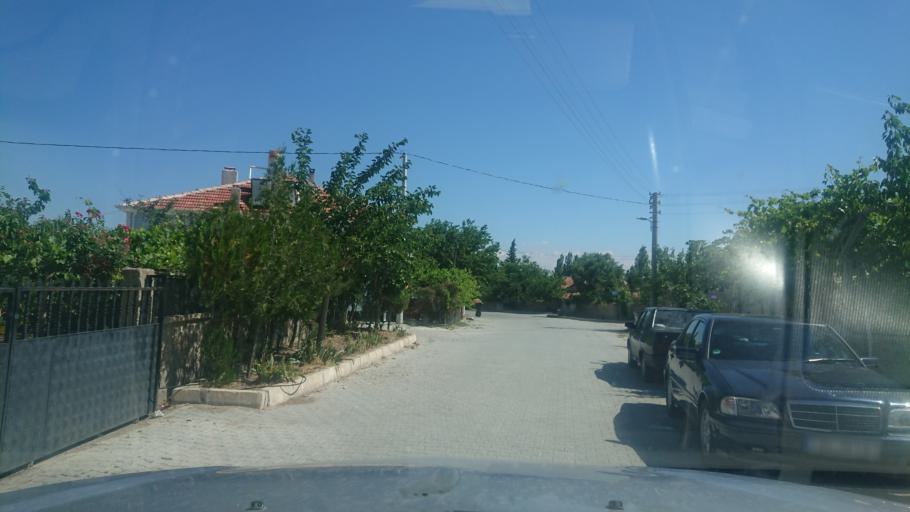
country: TR
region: Aksaray
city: Sariyahsi
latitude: 38.9853
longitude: 33.8455
